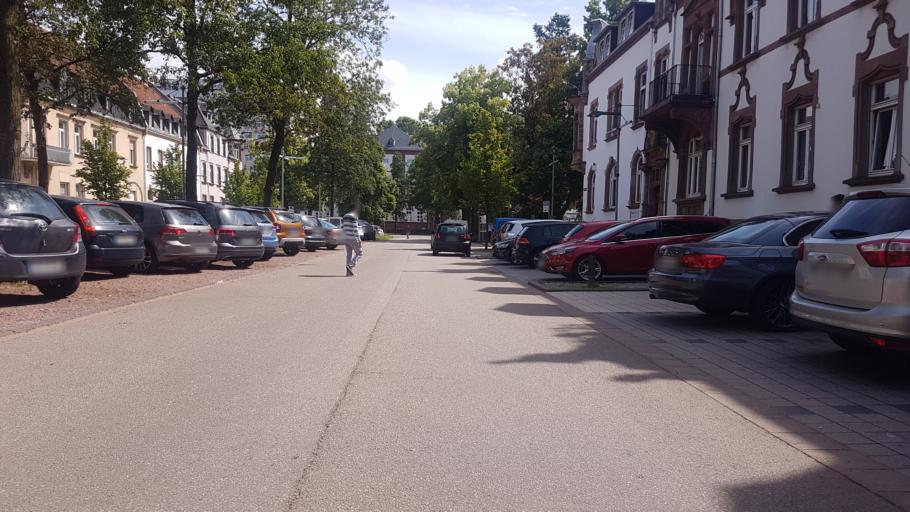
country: DE
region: Saarland
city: Saarlouis
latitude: 49.3135
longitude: 6.7546
